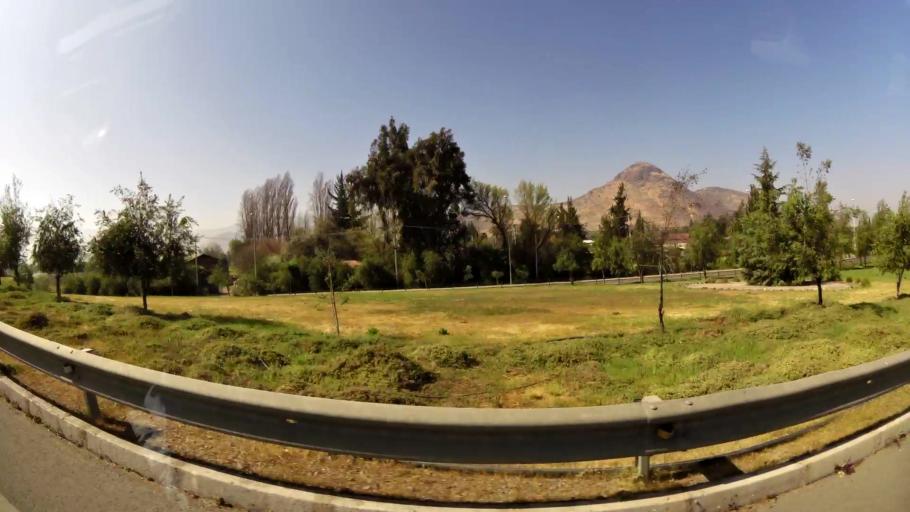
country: CL
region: Santiago Metropolitan
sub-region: Provincia de Chacabuco
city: Chicureo Abajo
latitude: -33.2919
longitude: -70.7013
